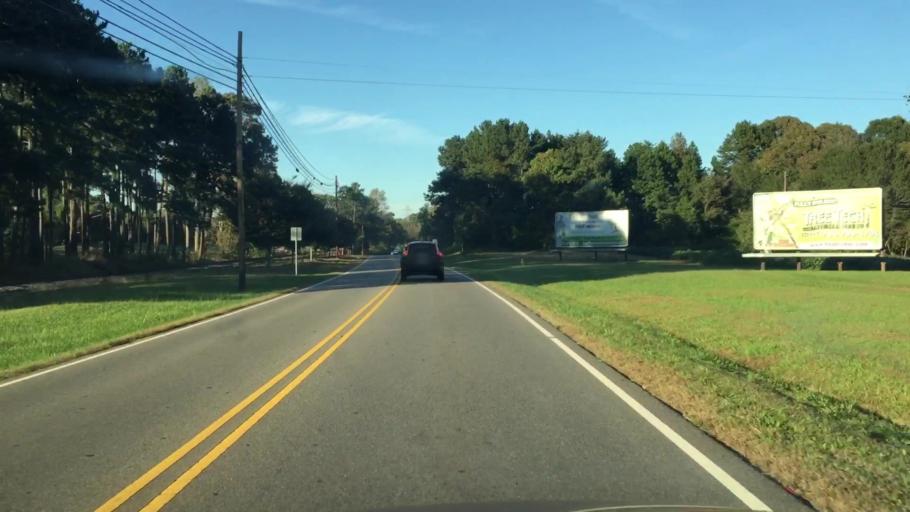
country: US
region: North Carolina
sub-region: Iredell County
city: Mooresville
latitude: 35.5671
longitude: -80.8282
